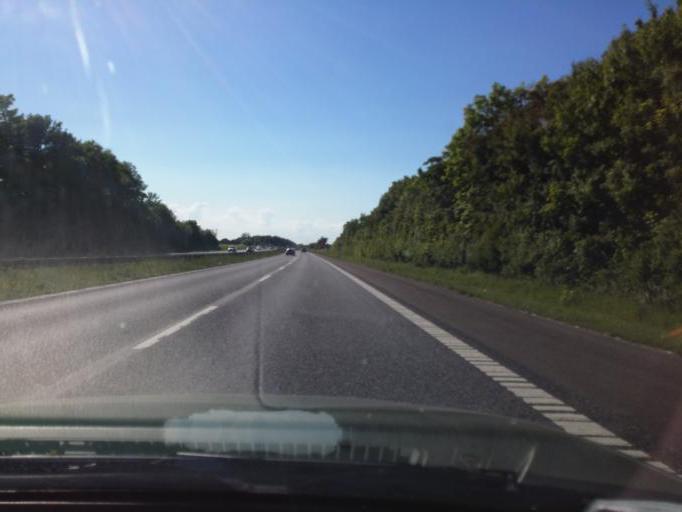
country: DK
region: South Denmark
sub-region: Middelfart Kommune
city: Ejby
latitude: 55.4617
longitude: 9.9202
